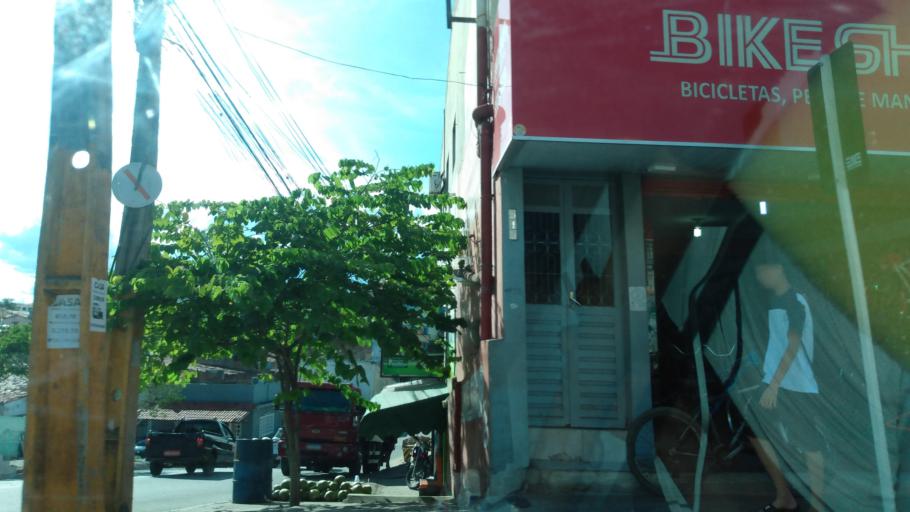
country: ET
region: Oromiya
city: Gore
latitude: 8.1990
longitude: 35.5626
